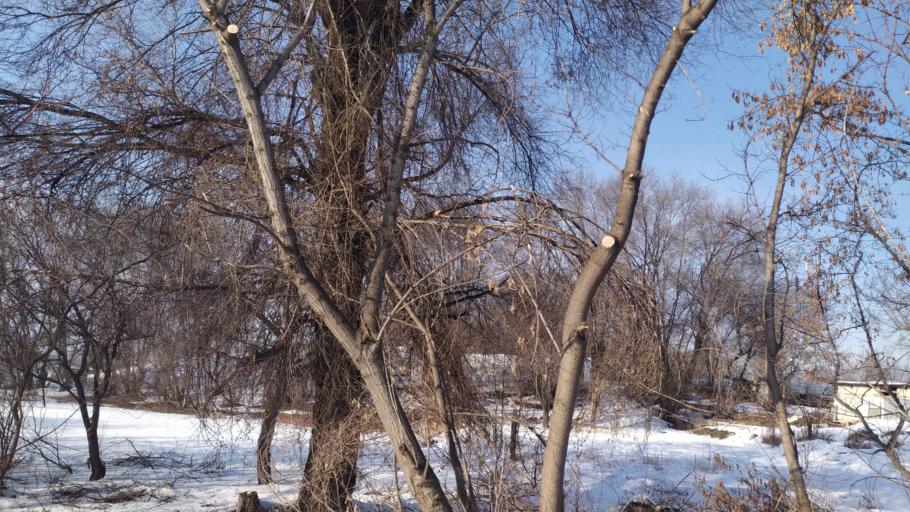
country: KZ
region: Almaty Oblysy
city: Burunday
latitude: 43.2431
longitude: 76.4309
